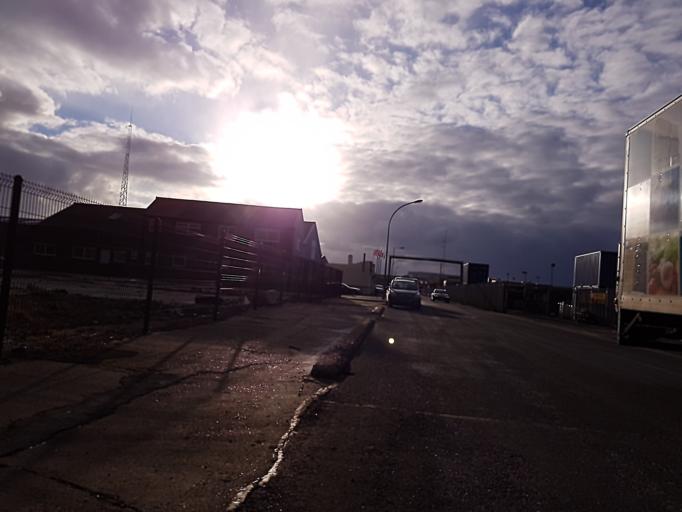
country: GB
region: England
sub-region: North East Lincolnshire
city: Grimsby
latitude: 53.5799
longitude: -0.0596
